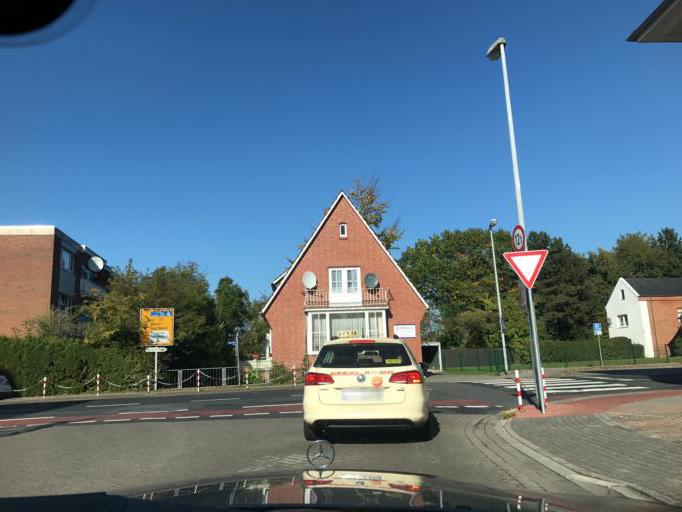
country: DE
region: Lower Saxony
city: Papenburg
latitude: 53.0845
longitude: 7.3881
